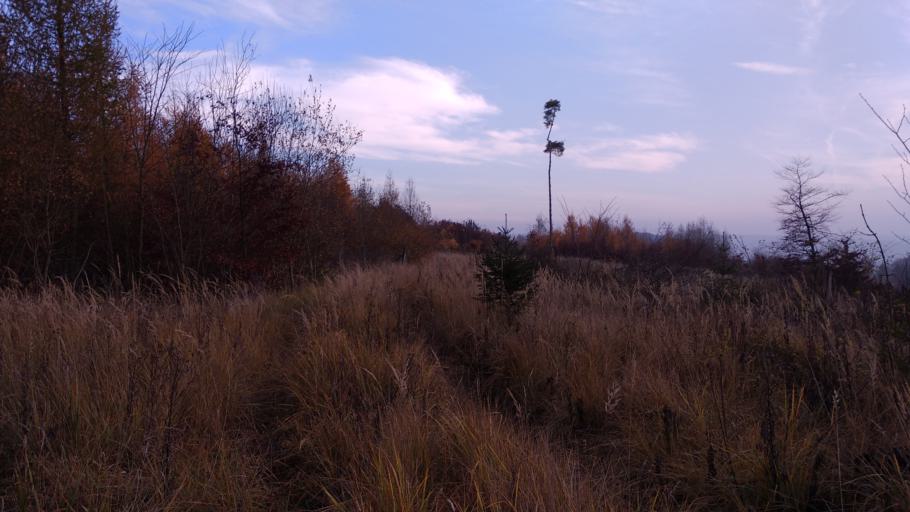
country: DE
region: North Rhine-Westphalia
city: Beverungen
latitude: 51.6690
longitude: 9.3322
